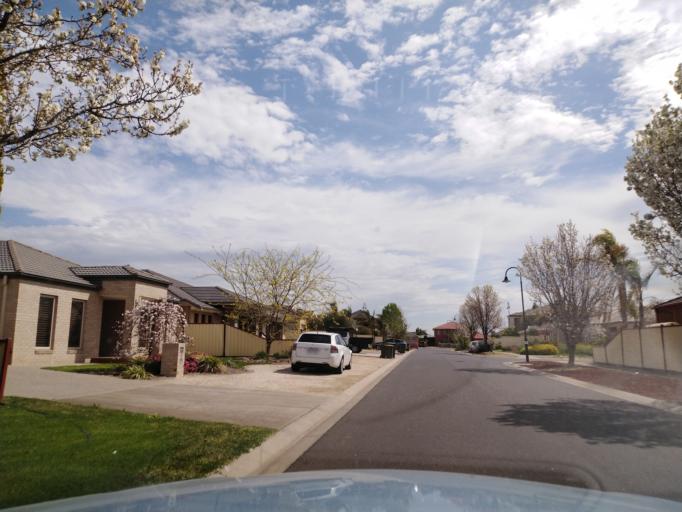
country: AU
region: Victoria
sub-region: Wyndham
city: Hoppers Crossing
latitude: -37.8486
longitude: 144.7083
